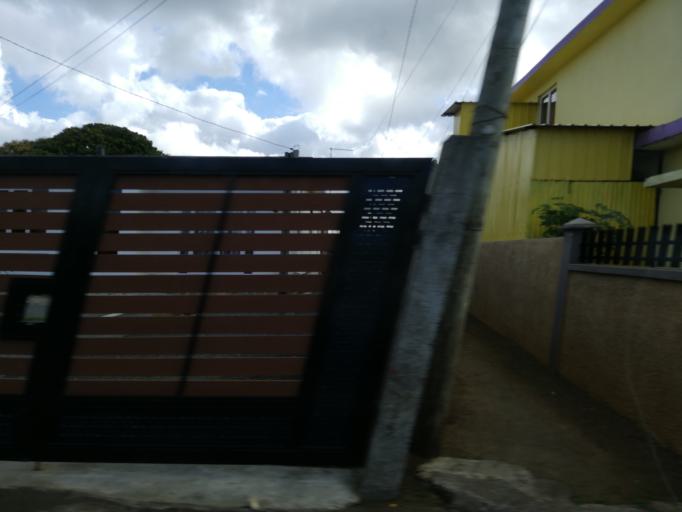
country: MU
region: Flacq
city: Camp de Masque
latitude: -20.2346
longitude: 57.6802
